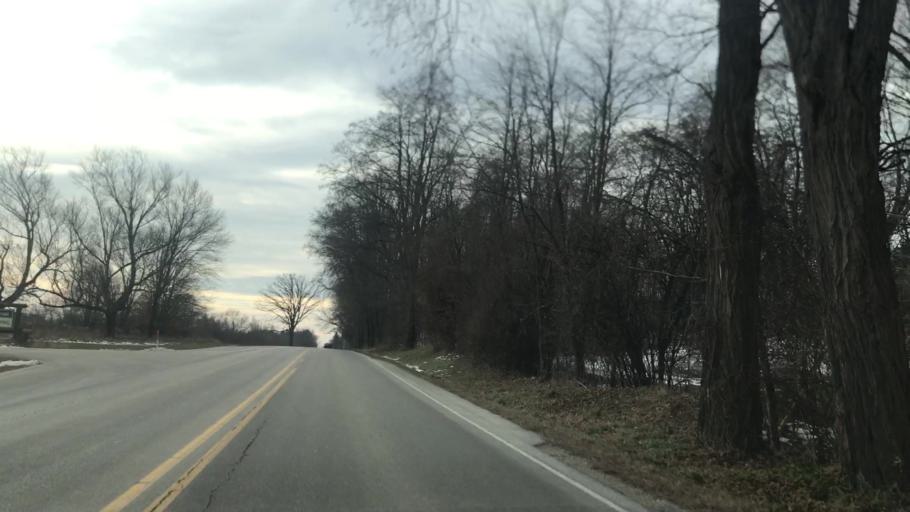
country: US
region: Wisconsin
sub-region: Waukesha County
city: Lannon
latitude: 43.1609
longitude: -88.1835
